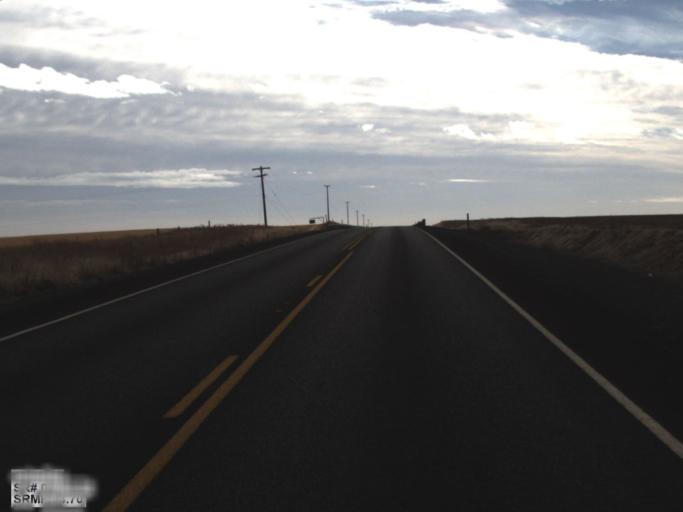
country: US
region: Washington
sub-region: Okanogan County
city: Coulee Dam
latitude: 47.7959
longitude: -118.7218
